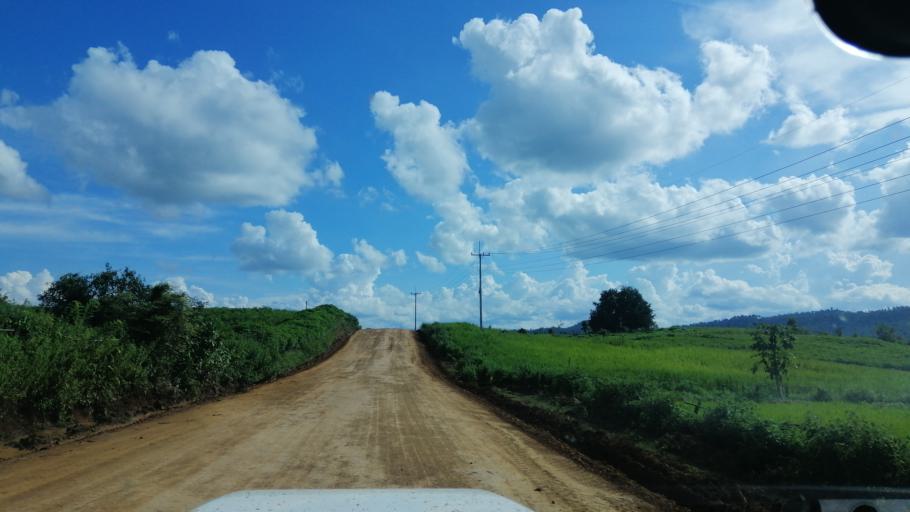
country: TH
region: Uttaradit
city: Ban Khok
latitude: 17.8908
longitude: 101.2166
